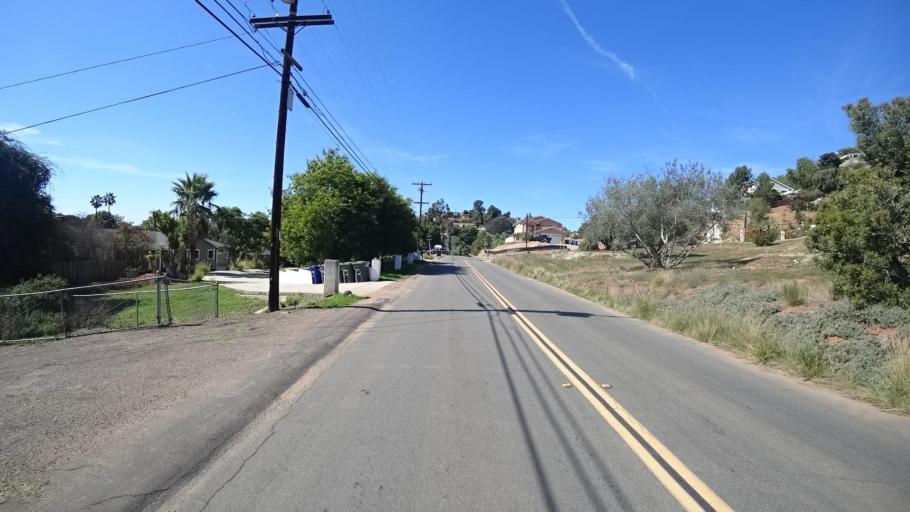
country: US
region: California
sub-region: San Diego County
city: Casa de Oro-Mount Helix
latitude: 32.7556
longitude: -116.9704
